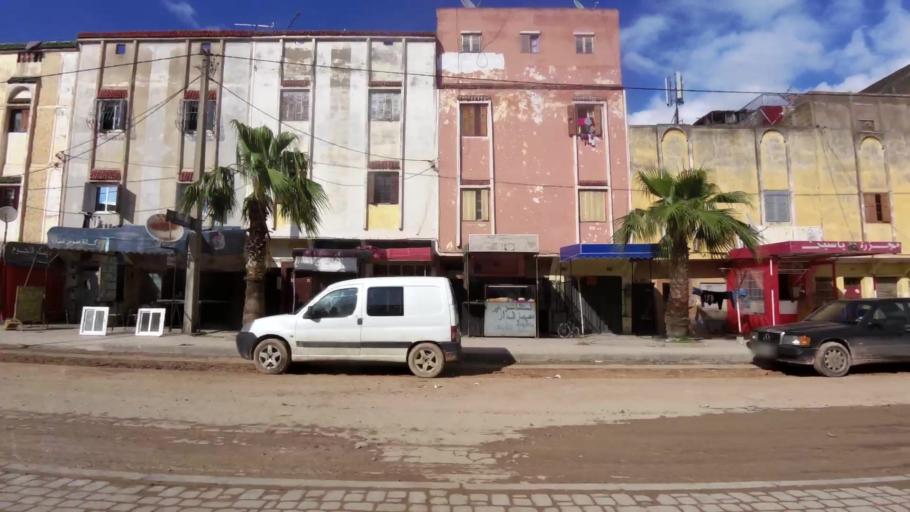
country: MA
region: Chaouia-Ouardigha
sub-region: Settat Province
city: Berrechid
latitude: 33.2736
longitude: -7.5734
